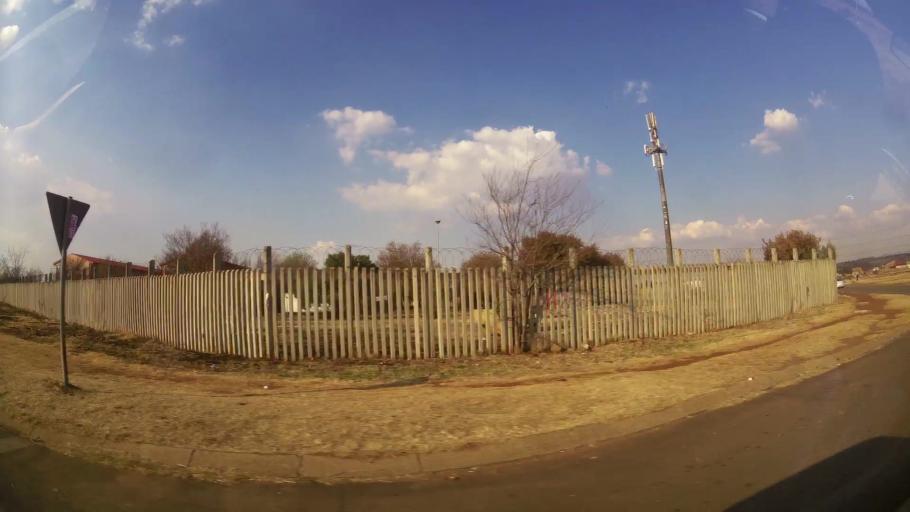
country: ZA
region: Gauteng
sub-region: Ekurhuleni Metropolitan Municipality
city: Germiston
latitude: -26.3701
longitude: 28.2183
